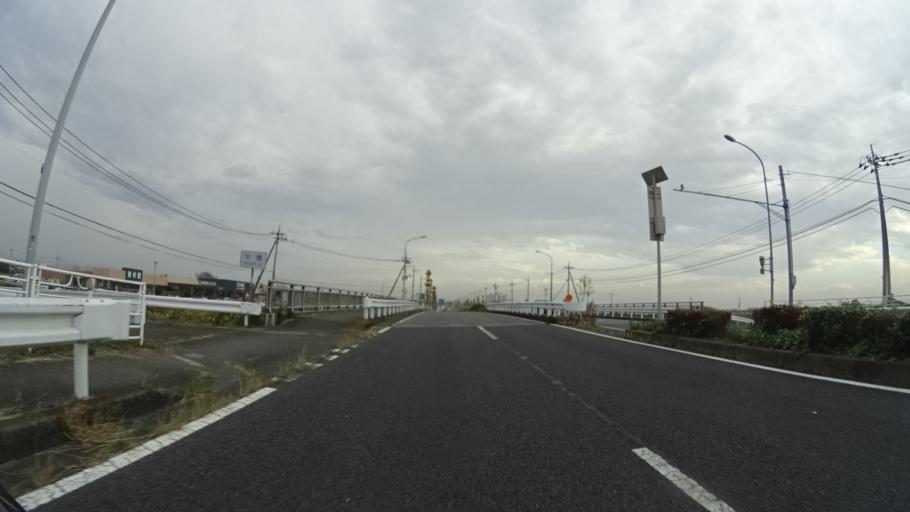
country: JP
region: Gunma
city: Maebashi-shi
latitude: 36.3727
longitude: 139.1307
